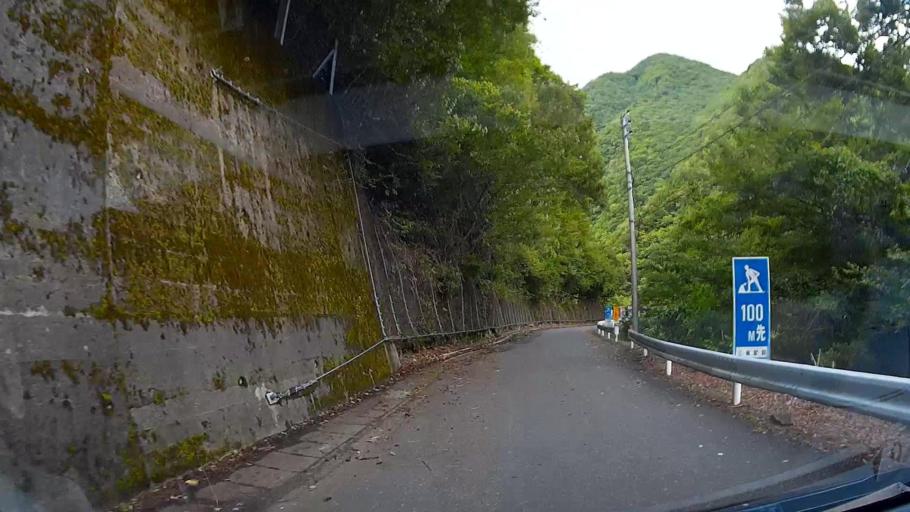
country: JP
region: Shizuoka
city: Shizuoka-shi
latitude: 35.3056
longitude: 138.2141
